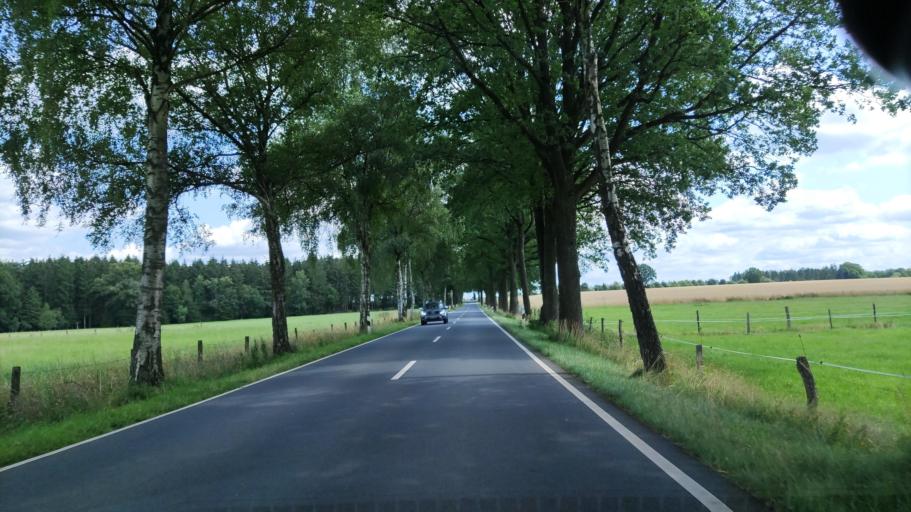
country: DE
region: Lower Saxony
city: Walsrode
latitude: 52.9159
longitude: 9.5603
